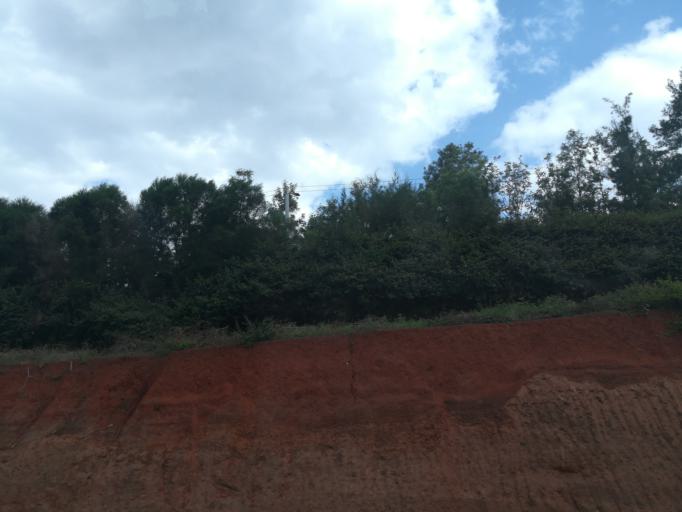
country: KE
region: Nairobi Area
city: Nairobi
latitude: -1.3178
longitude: 36.7721
